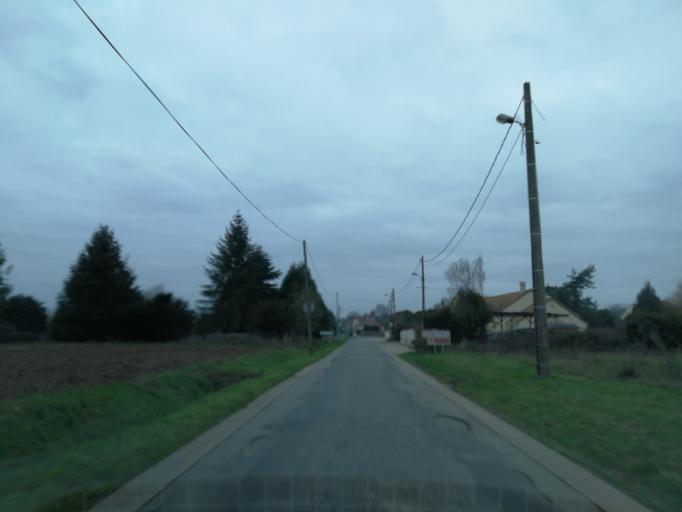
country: FR
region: Ile-de-France
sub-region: Departement de l'Essonne
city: Les Molieres
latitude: 48.6687
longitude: 2.0715
